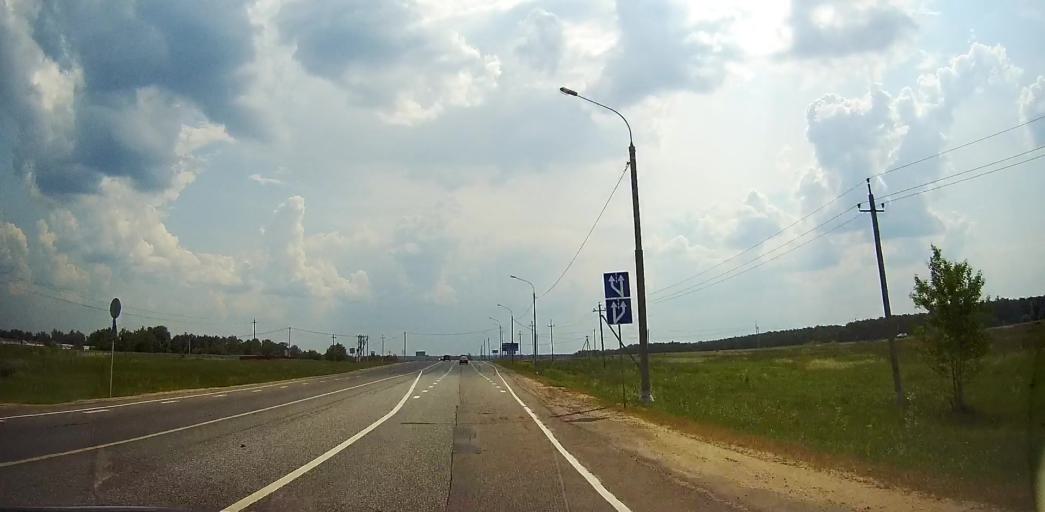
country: RU
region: Moskovskaya
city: Stupino
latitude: 54.9579
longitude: 38.1240
